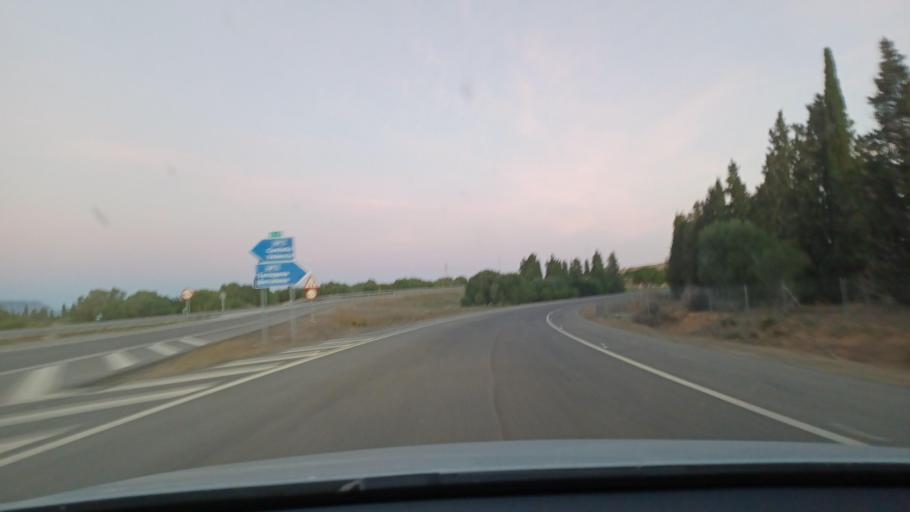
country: ES
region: Catalonia
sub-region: Provincia de Tarragona
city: Amposta
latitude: 40.7292
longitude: 0.5865
